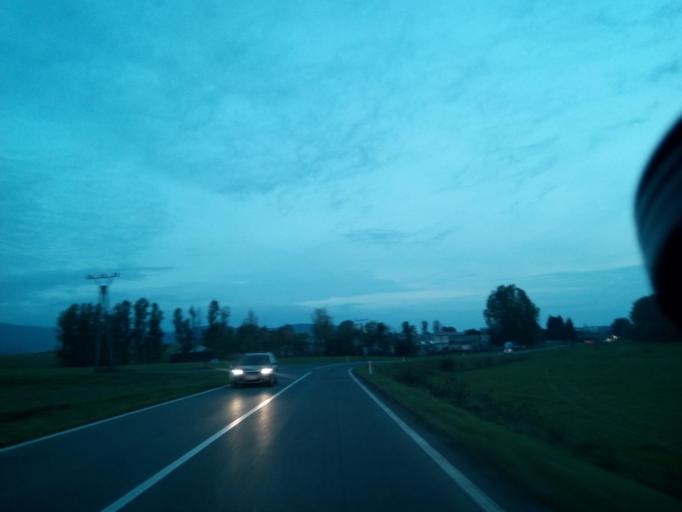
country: SK
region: Presovsky
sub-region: Okres Presov
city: Presov
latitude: 49.0595
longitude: 21.3452
